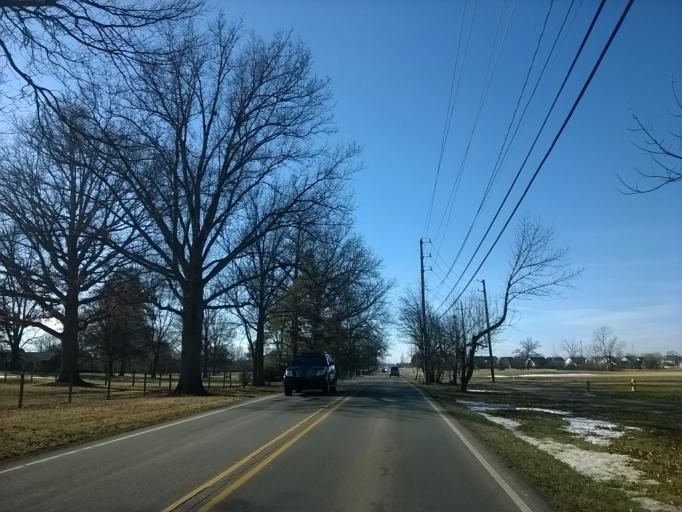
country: US
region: Indiana
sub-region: Boone County
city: Zionsville
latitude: 39.9409
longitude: -86.2276
